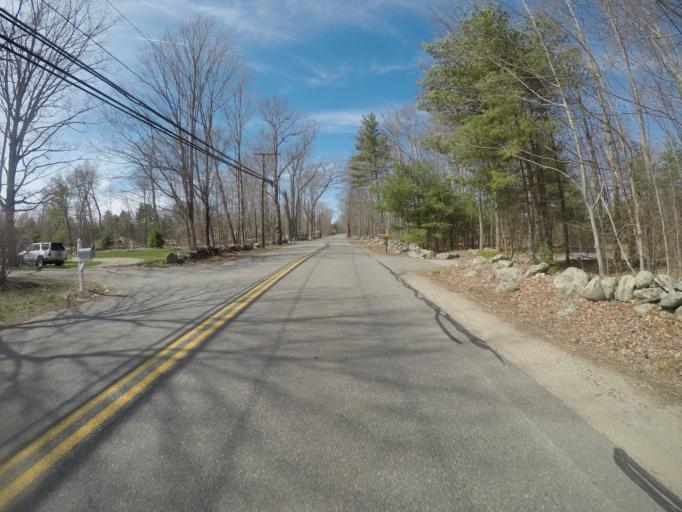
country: US
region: Massachusetts
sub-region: Bristol County
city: Easton
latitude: 42.0305
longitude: -71.0863
